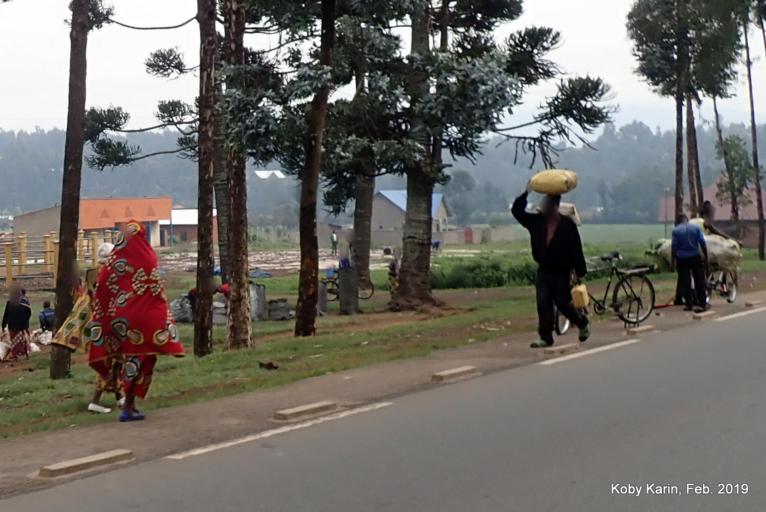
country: RW
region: Northern Province
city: Musanze
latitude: -1.5270
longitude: 29.5736
